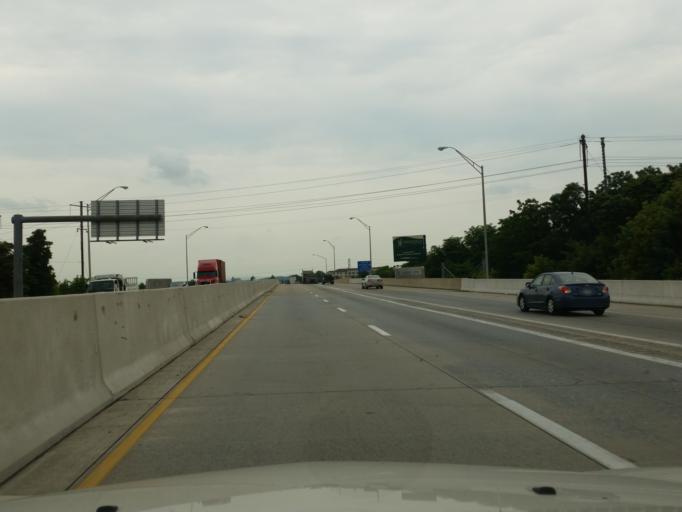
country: US
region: Pennsylvania
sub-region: Lancaster County
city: Lampeter
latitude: 40.0421
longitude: -76.2466
